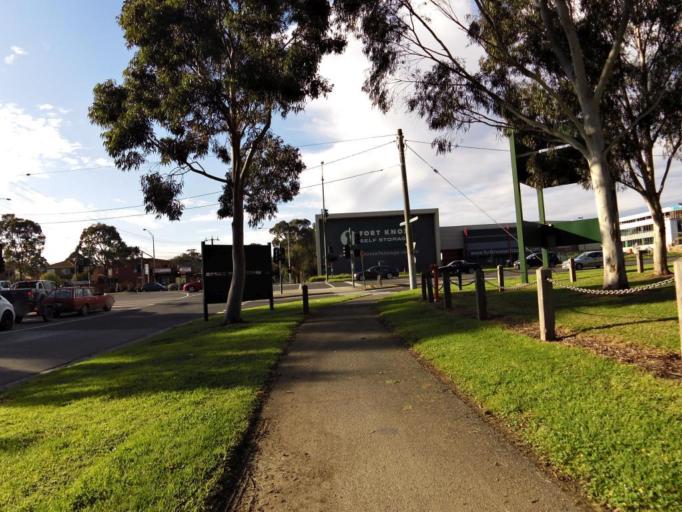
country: AU
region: Victoria
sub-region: Whitehorse
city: Vermont South
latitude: -37.8592
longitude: 145.1980
